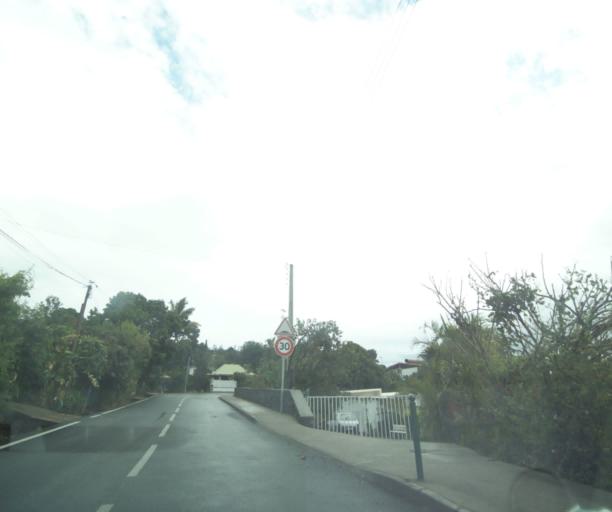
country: RE
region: Reunion
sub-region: Reunion
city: Saint-Paul
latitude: -21.0239
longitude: 55.2868
